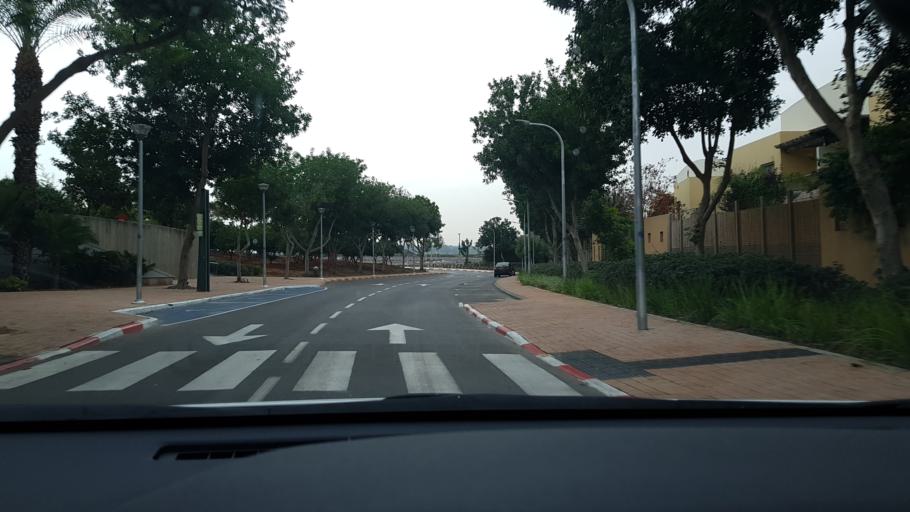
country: IL
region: Central District
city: Ness Ziona
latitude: 31.9071
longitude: 34.8201
